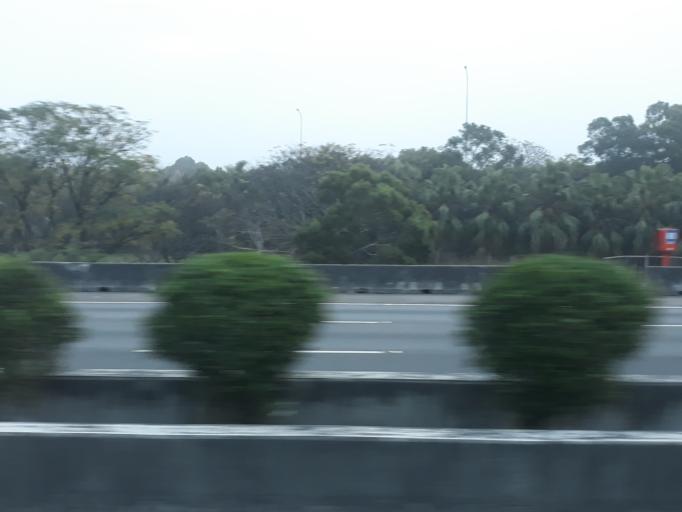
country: TW
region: Taiwan
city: Fengyuan
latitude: 24.3188
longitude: 120.7052
